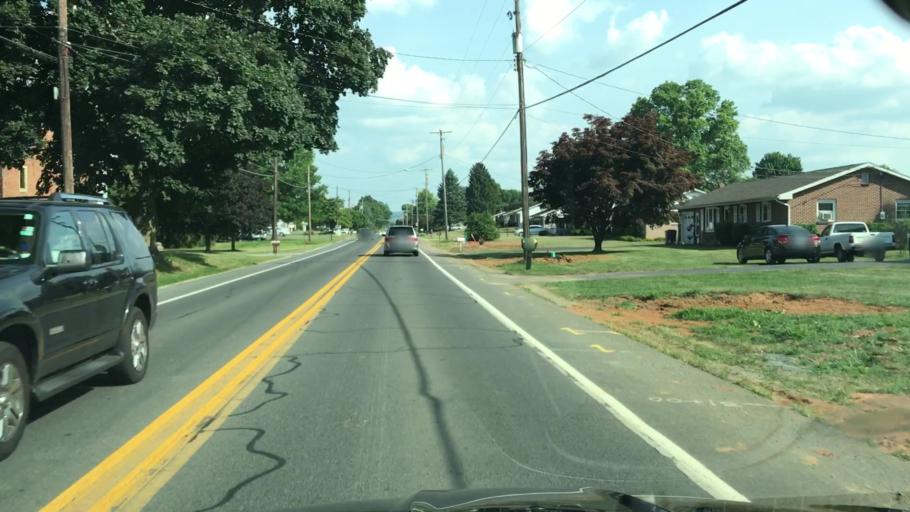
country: US
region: Pennsylvania
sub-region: Cumberland County
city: Carlisle
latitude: 40.1848
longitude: -77.1568
